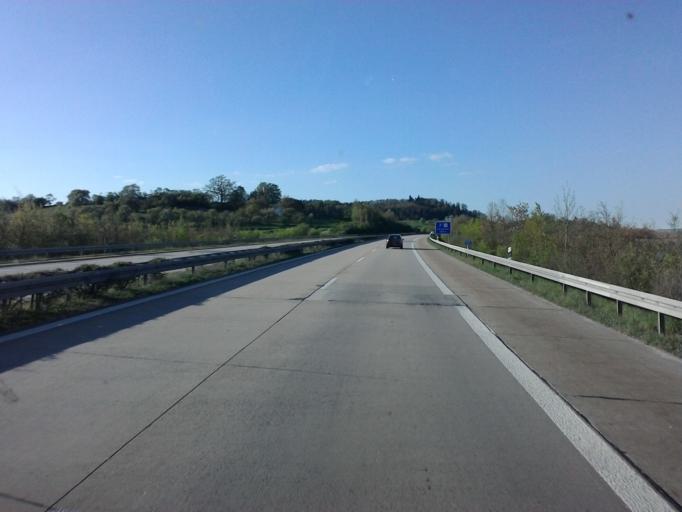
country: DE
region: Bavaria
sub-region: Regierungsbezirk Mittelfranken
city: Schnelldorf
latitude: 49.2340
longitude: 10.2127
